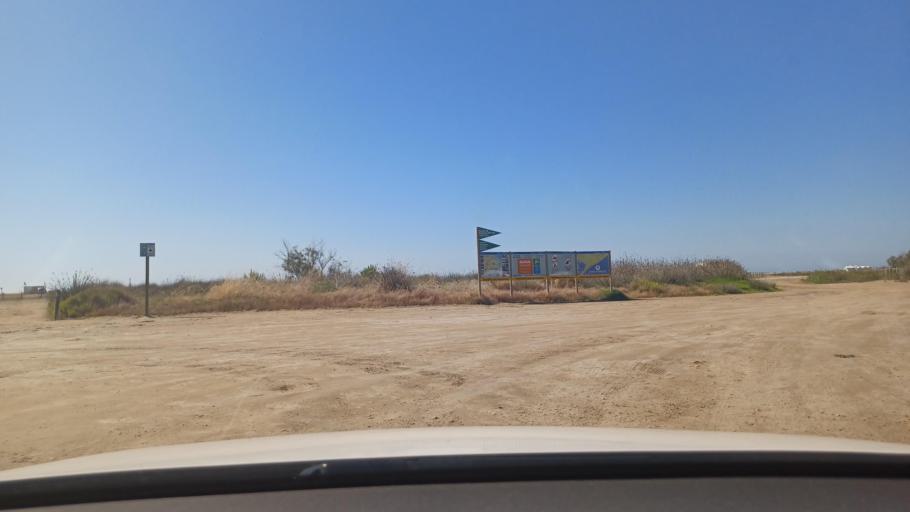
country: ES
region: Catalonia
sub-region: Provincia de Tarragona
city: Deltebre
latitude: 40.6557
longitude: 0.7830
